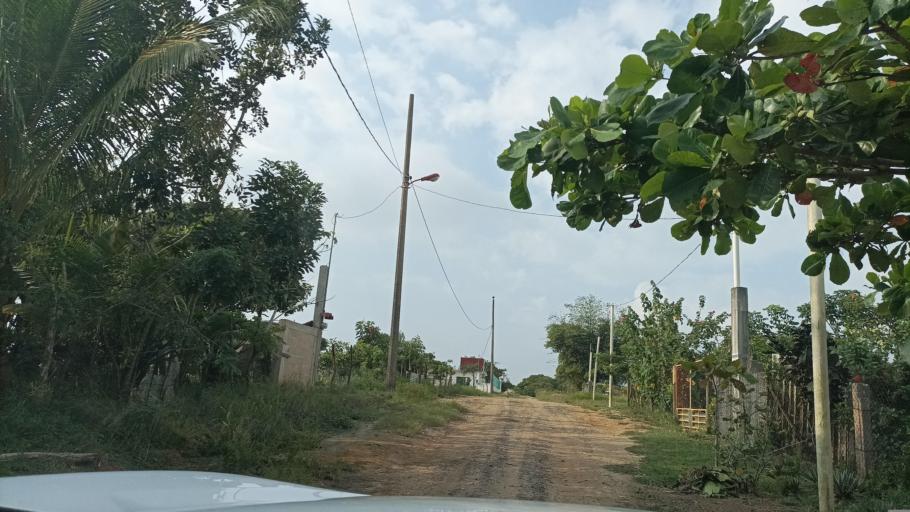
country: MX
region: Veracruz
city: Allende
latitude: 18.1561
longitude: -94.3267
